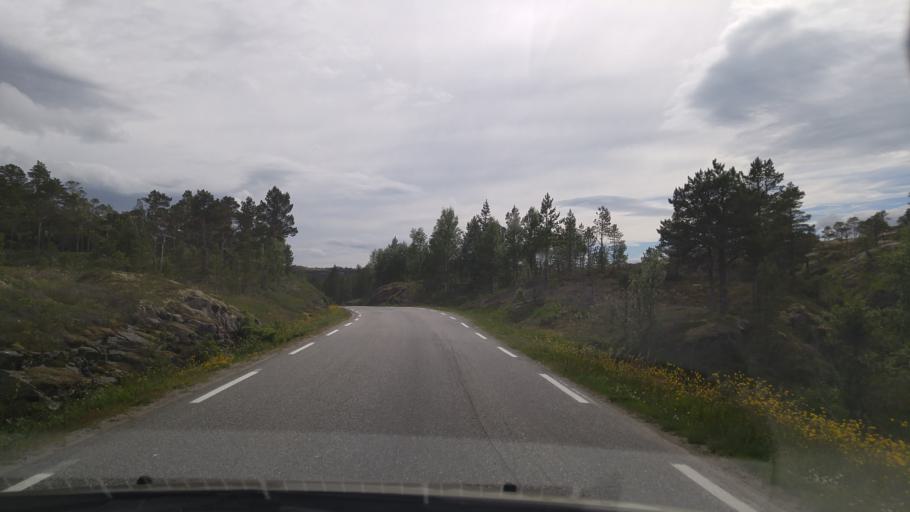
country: NO
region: Nord-Trondelag
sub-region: Namsos
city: Namsos
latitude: 64.6427
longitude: 11.4477
